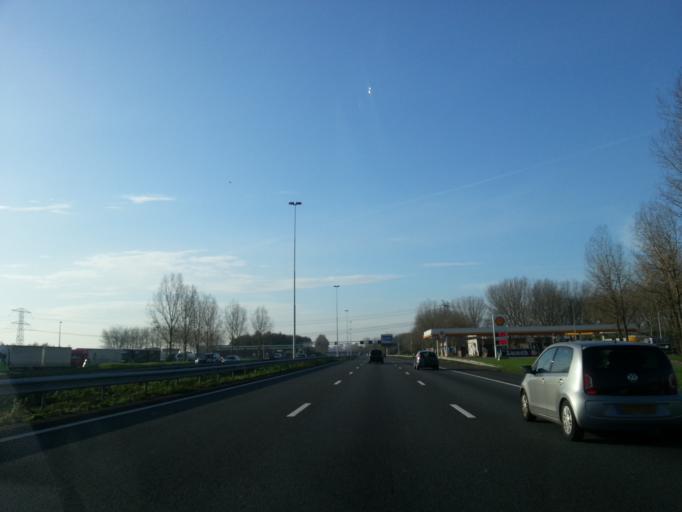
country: NL
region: South Holland
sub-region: Gemeente Capelle aan den IJssel
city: Capelle aan den IJssel
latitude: 51.9680
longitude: 4.5914
